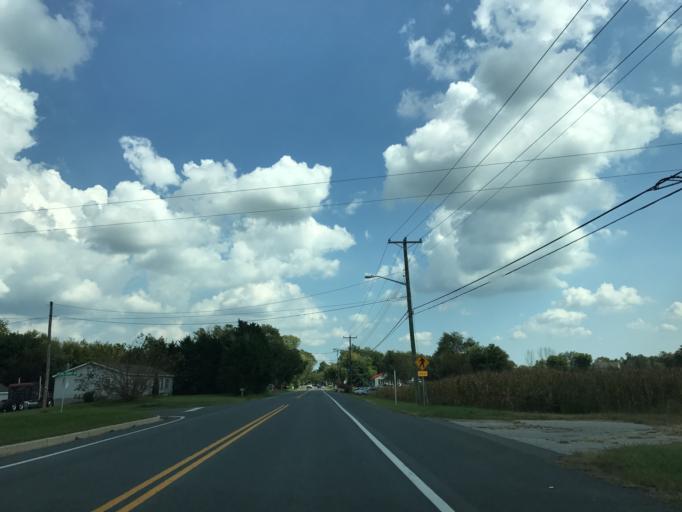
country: US
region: Maryland
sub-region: Caroline County
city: Greensboro
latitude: 39.1354
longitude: -75.7715
